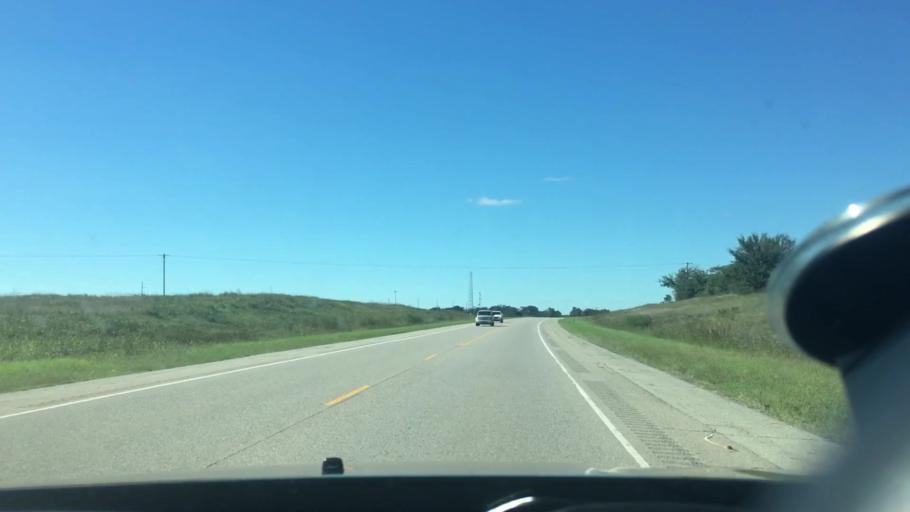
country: US
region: Oklahoma
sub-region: Coal County
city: Coalgate
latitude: 34.6132
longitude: -96.4393
